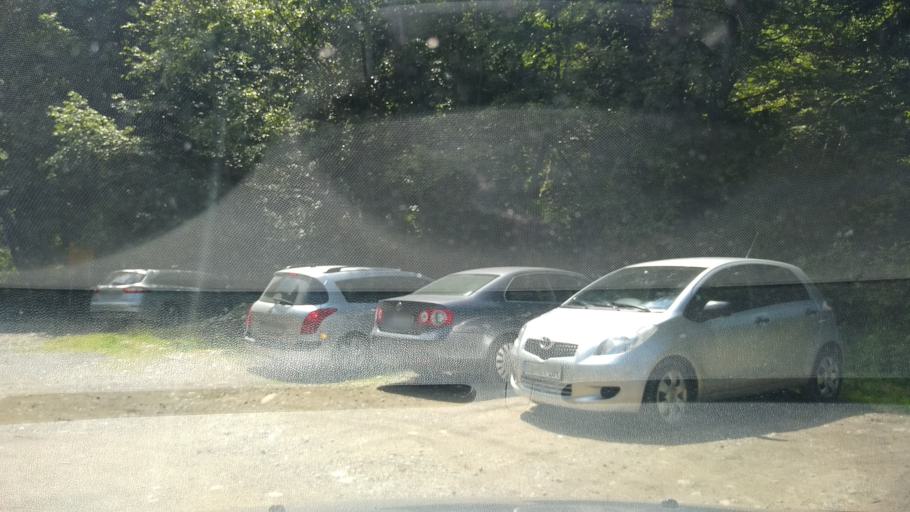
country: RO
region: Hunedoara
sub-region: Comuna Rau de Mori
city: Rau de Mori
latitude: 45.4323
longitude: 22.8949
